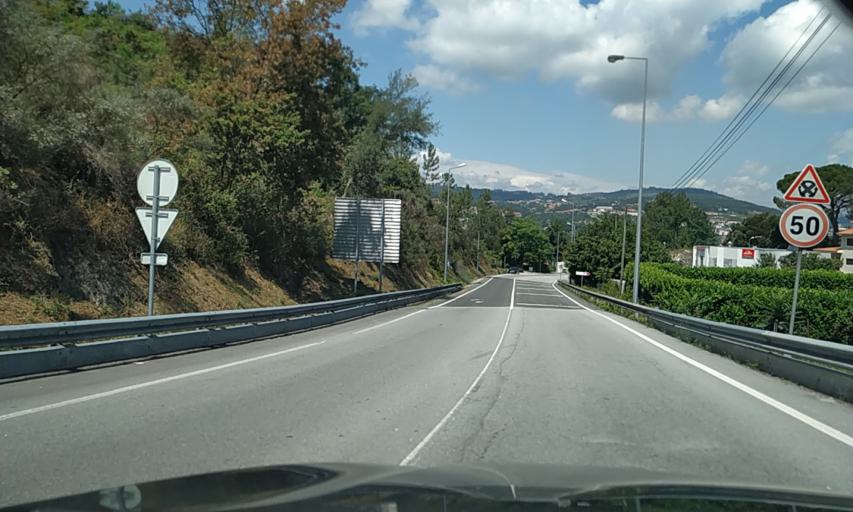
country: PT
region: Porto
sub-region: Amarante
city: Amarante
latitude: 41.2641
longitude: -8.0741
